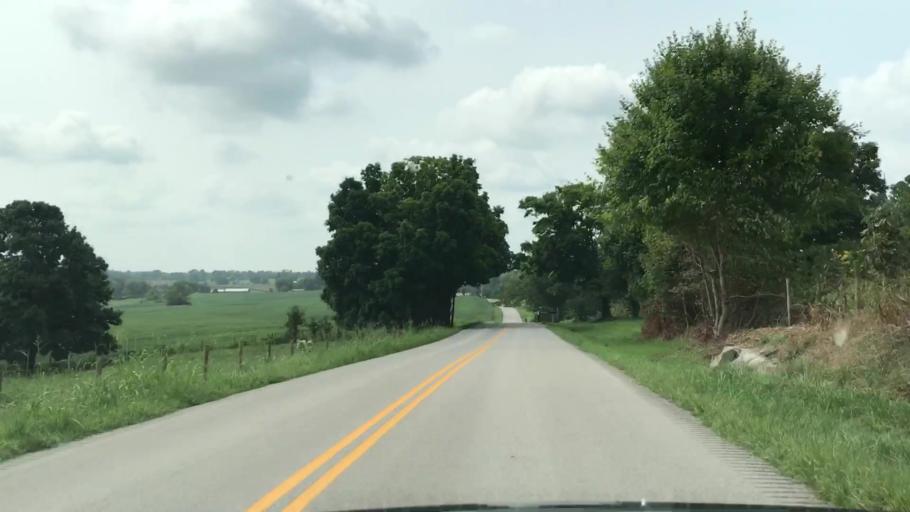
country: US
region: Kentucky
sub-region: Edmonson County
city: Brownsville
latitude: 37.0997
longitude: -86.1470
